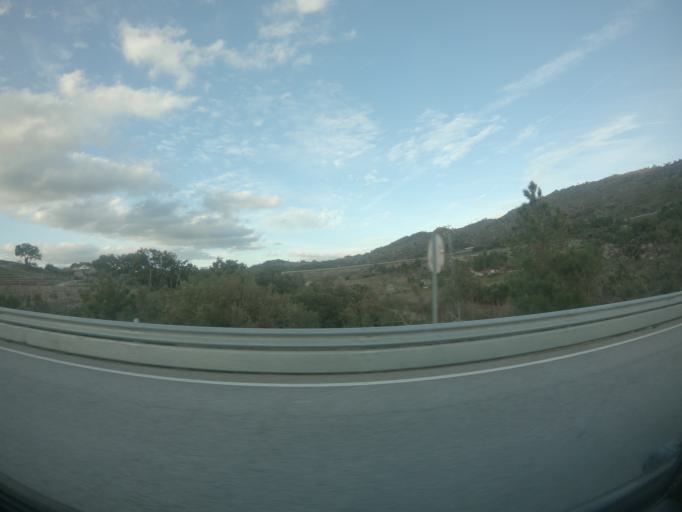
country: PT
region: Braganca
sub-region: Carrazeda de Ansiaes
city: Carrazeda de Anciaes
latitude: 41.2940
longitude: -7.3409
